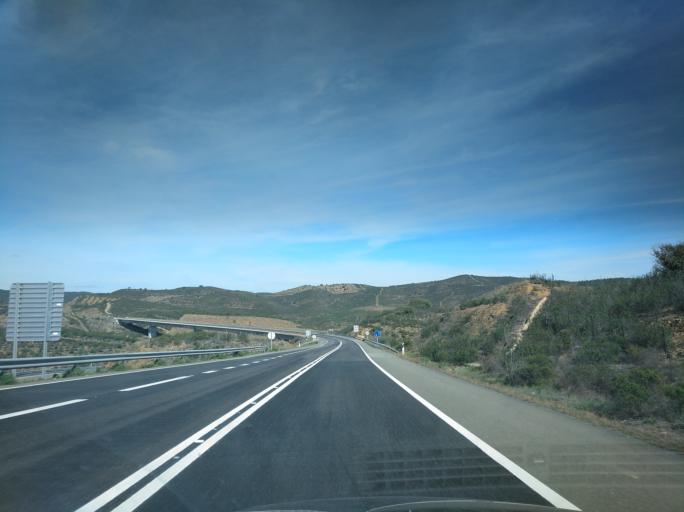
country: PT
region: Faro
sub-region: Alcoutim
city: Alcoutim
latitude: 37.3833
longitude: -7.5278
